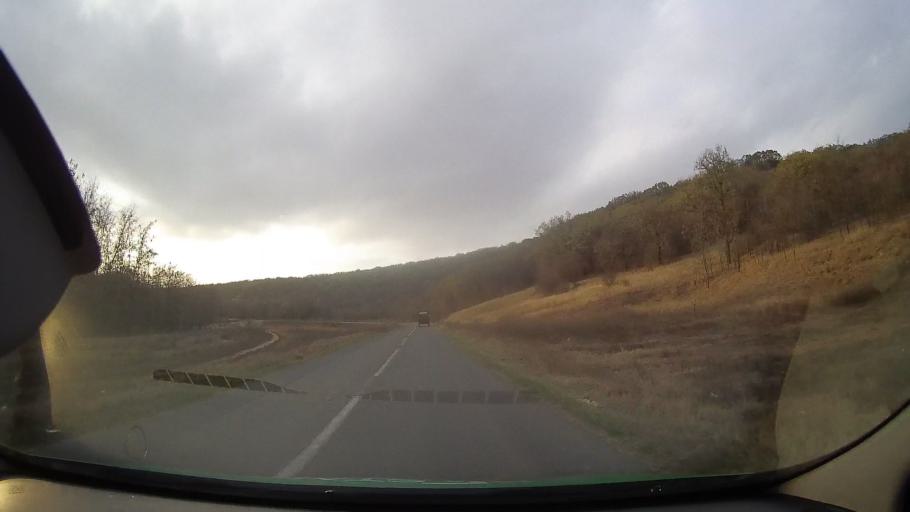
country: RO
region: Constanta
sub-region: Comuna Adamclisi
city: Adamclisi
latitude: 44.0397
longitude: 27.9461
